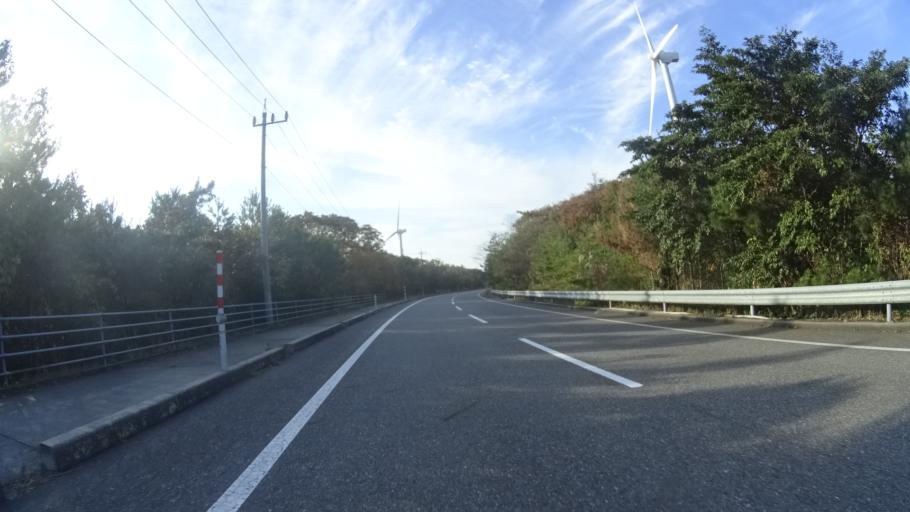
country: JP
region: Ishikawa
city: Hakui
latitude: 37.0712
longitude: 136.7368
